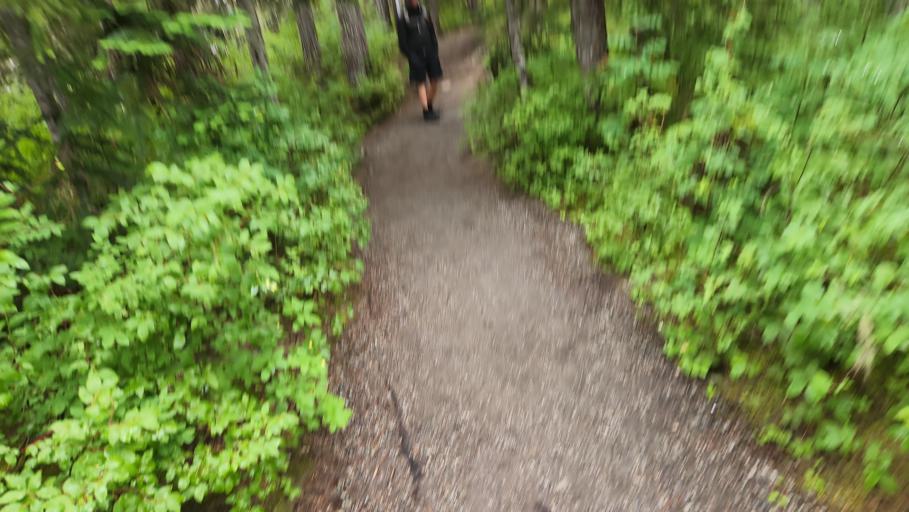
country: CA
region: British Columbia
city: Pemberton
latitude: 50.3674
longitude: -122.4996
